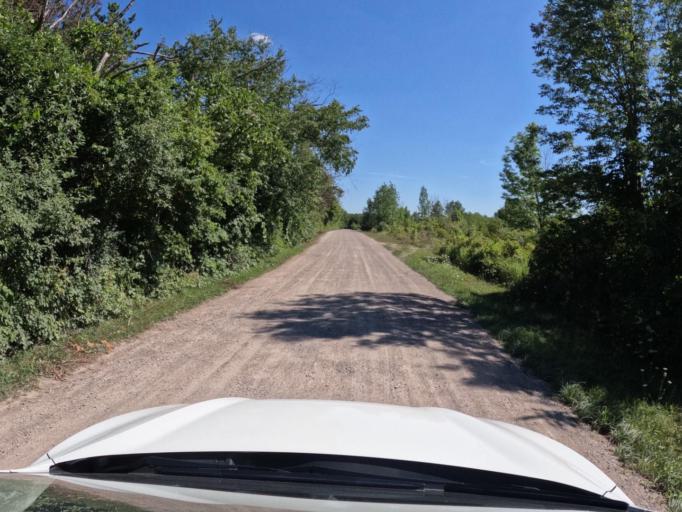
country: CA
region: Ontario
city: Cambridge
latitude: 43.4244
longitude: -80.2543
